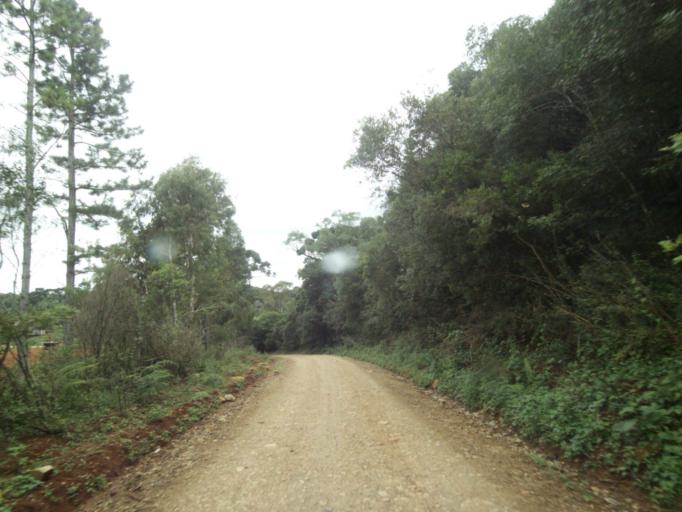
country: BR
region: Rio Grande do Sul
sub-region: Lagoa Vermelha
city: Lagoa Vermelha
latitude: -28.1989
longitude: -51.5355
